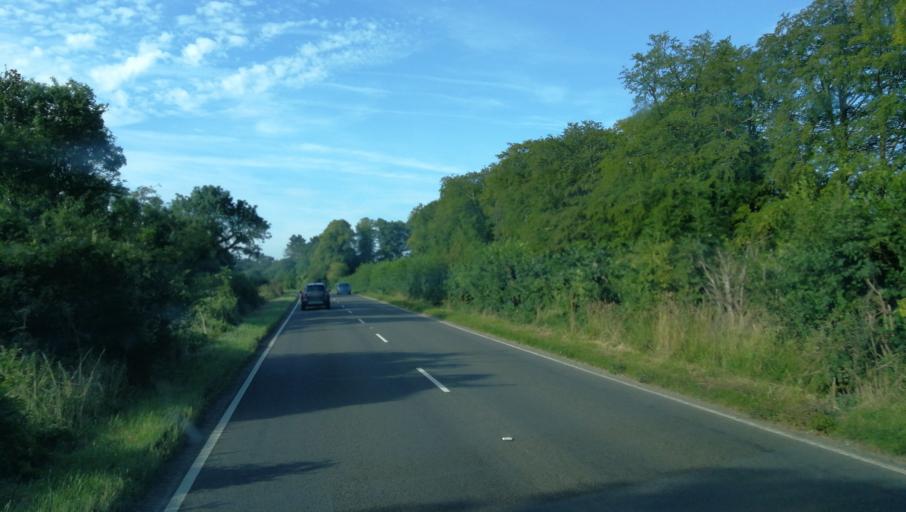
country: GB
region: England
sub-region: Oxfordshire
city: Somerton
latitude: 51.9140
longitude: -1.3270
